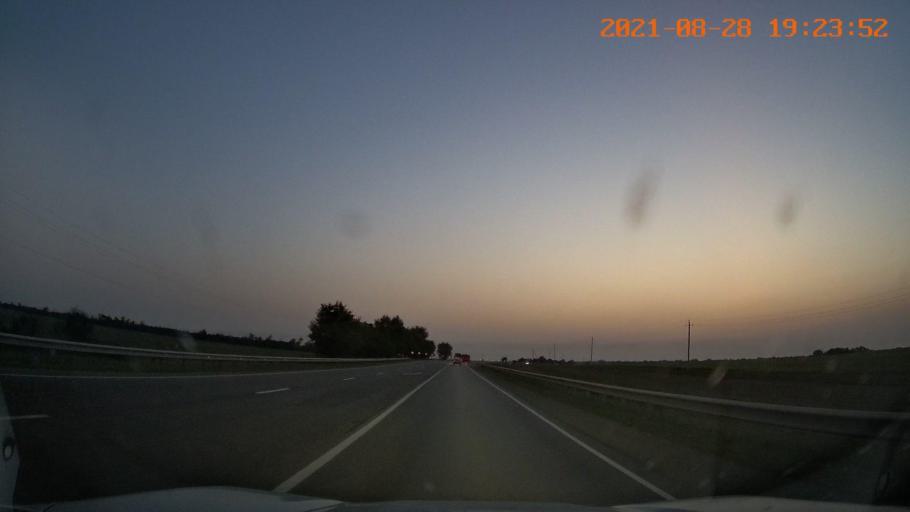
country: RU
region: Adygeya
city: Ponezhukay
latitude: 44.8735
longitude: 39.4427
